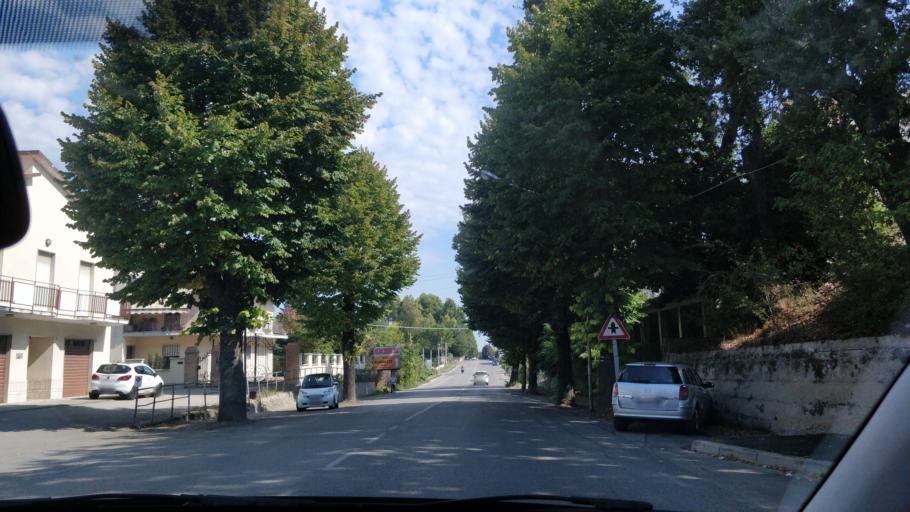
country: IT
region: Abruzzo
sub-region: Provincia di Chieti
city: Chieti
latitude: 42.3851
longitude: 14.1541
